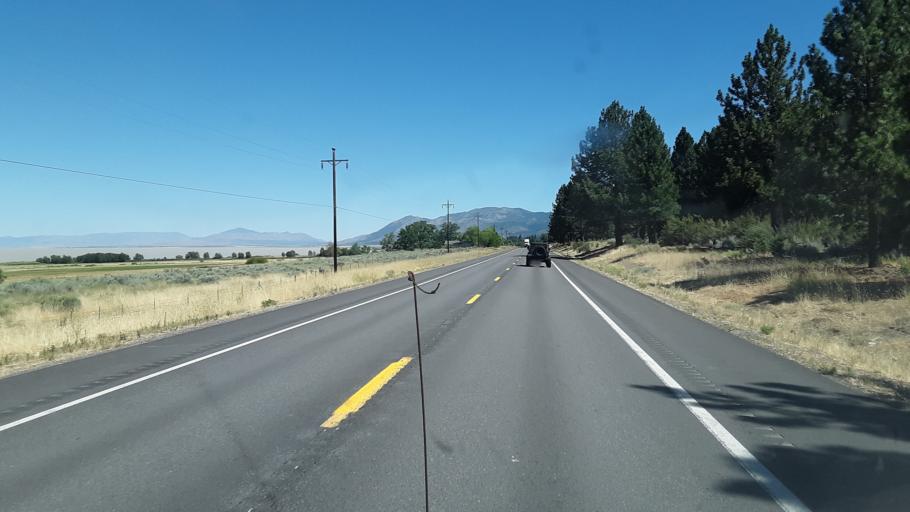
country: US
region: California
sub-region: Lassen County
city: Janesville
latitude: 40.2409
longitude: -120.4529
